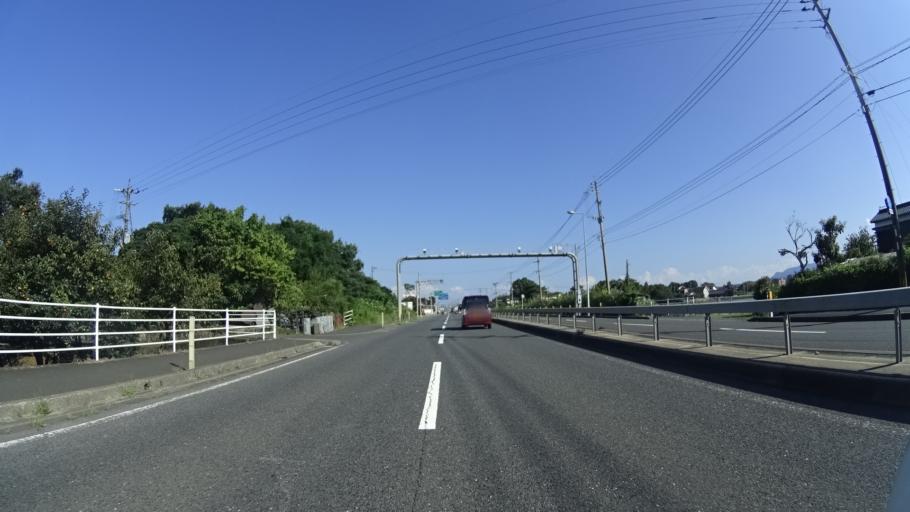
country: JP
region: Fukuoka
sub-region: Buzen-shi
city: Buzen
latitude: 33.6029
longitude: 131.1243
